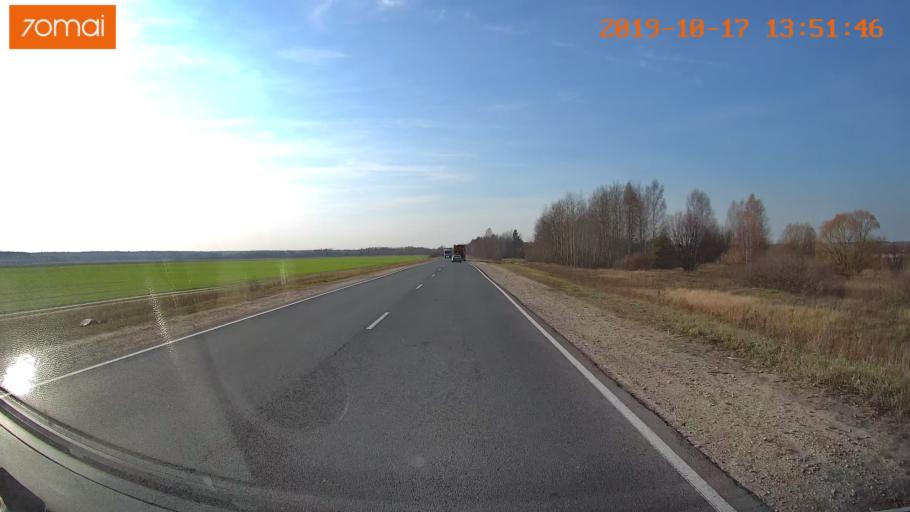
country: RU
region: Rjazan
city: Tuma
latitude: 55.1399
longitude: 40.3803
